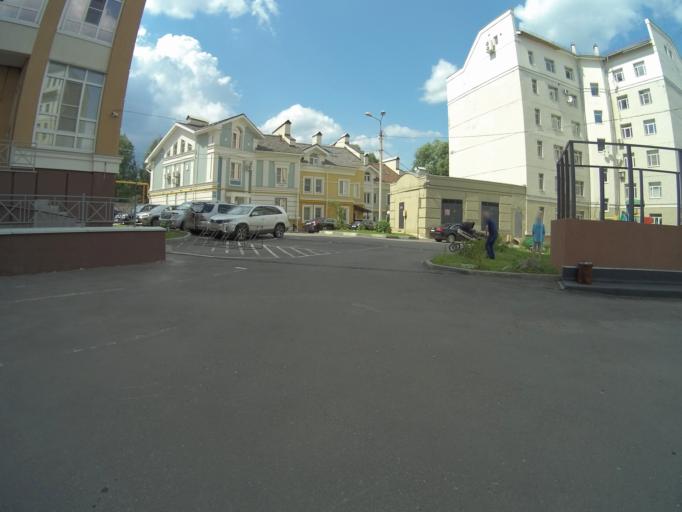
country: RU
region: Vladimir
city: Vladimir
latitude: 56.1321
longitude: 40.3903
